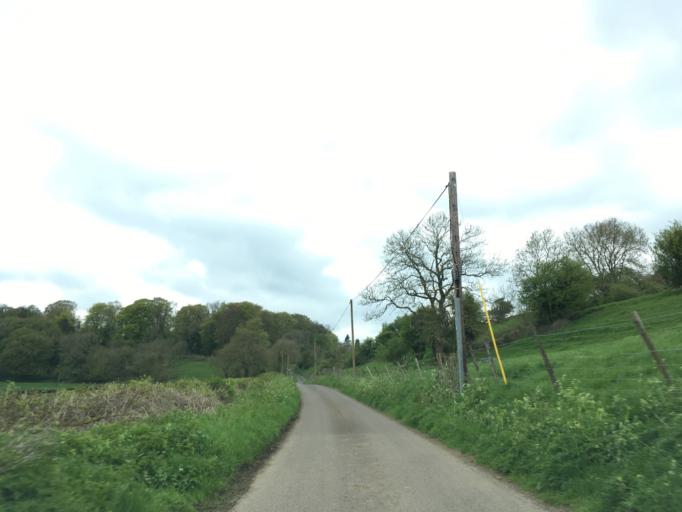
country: GB
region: England
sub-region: Gloucestershire
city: Wotton-under-Edge
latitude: 51.6407
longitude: -2.3014
